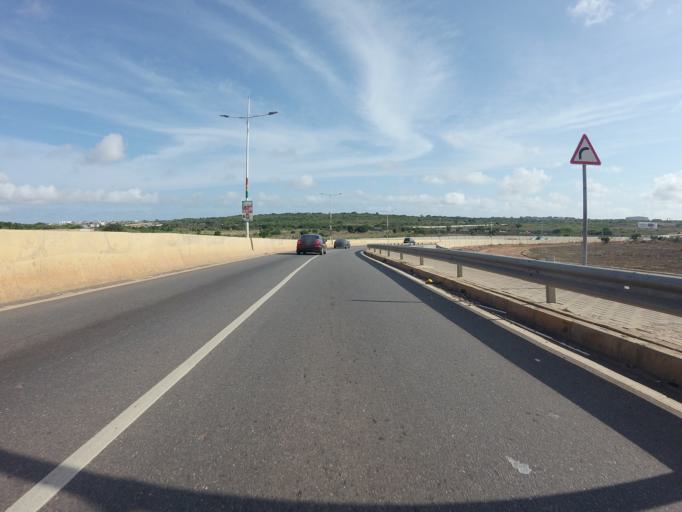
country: GH
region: Greater Accra
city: Medina Estates
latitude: 5.6185
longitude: -0.1527
